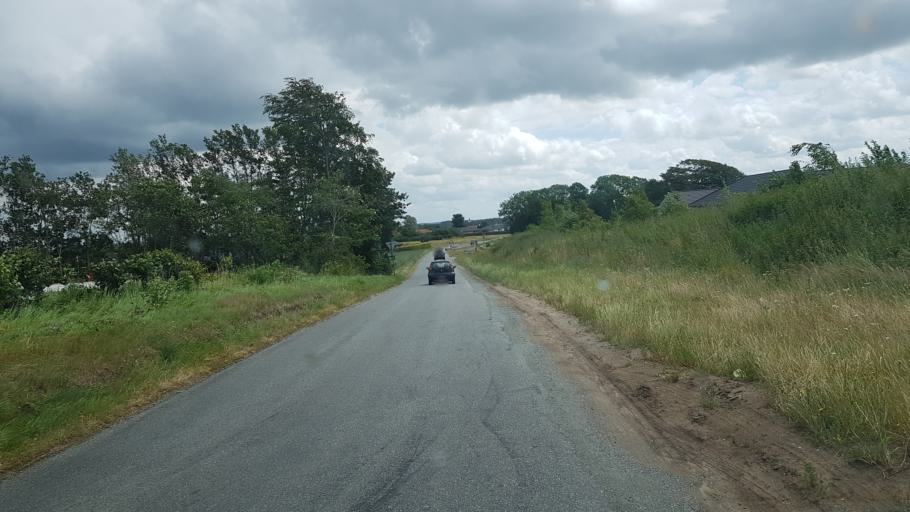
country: DK
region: South Denmark
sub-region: Kolding Kommune
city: Lunderskov
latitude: 55.4838
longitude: 9.2754
